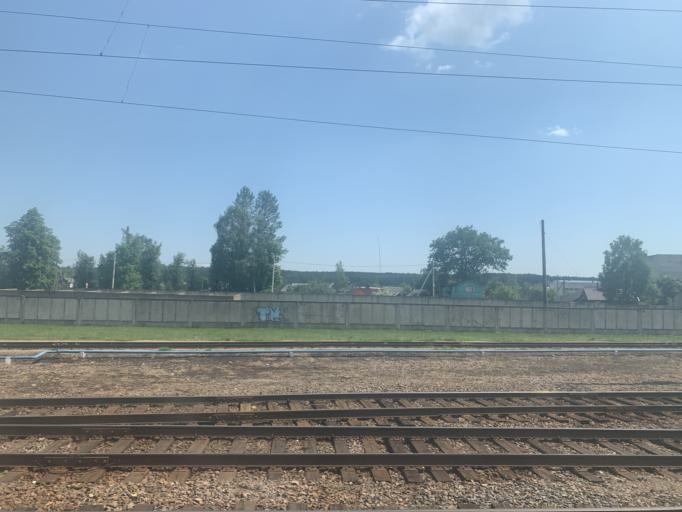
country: BY
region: Minsk
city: Stowbtsy
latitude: 53.4865
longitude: 26.7621
